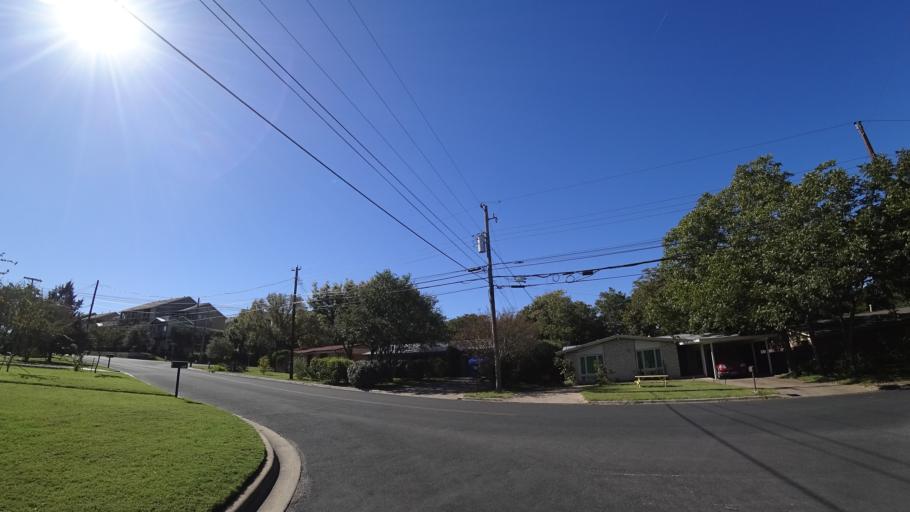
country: US
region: Texas
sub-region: Travis County
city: Rollingwood
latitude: 30.2455
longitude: -97.7756
